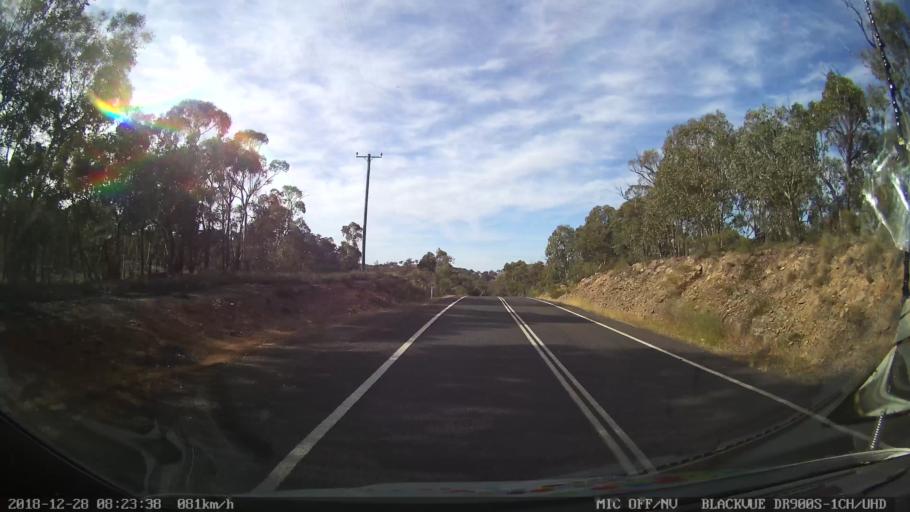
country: AU
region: New South Wales
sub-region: Blayney
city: Blayney
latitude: -33.9095
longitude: 149.3472
